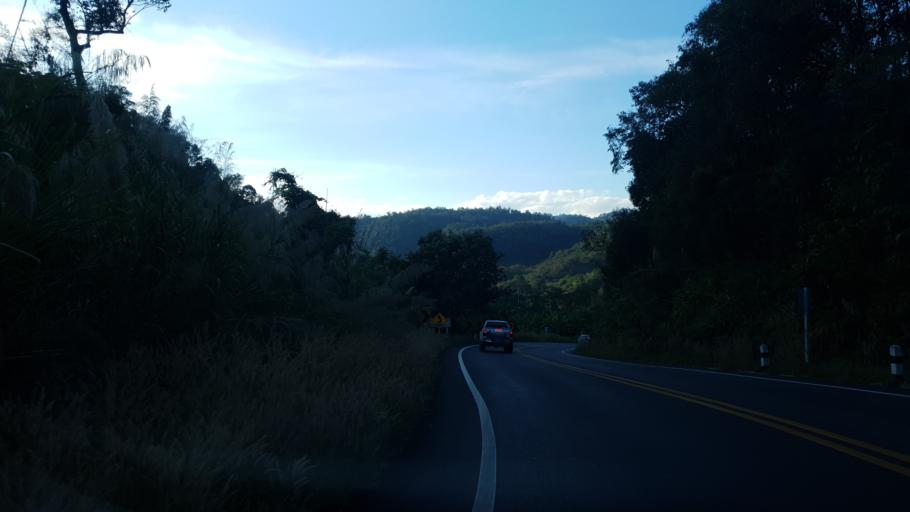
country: TH
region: Loei
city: Dan Sai
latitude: 17.2294
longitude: 101.0573
